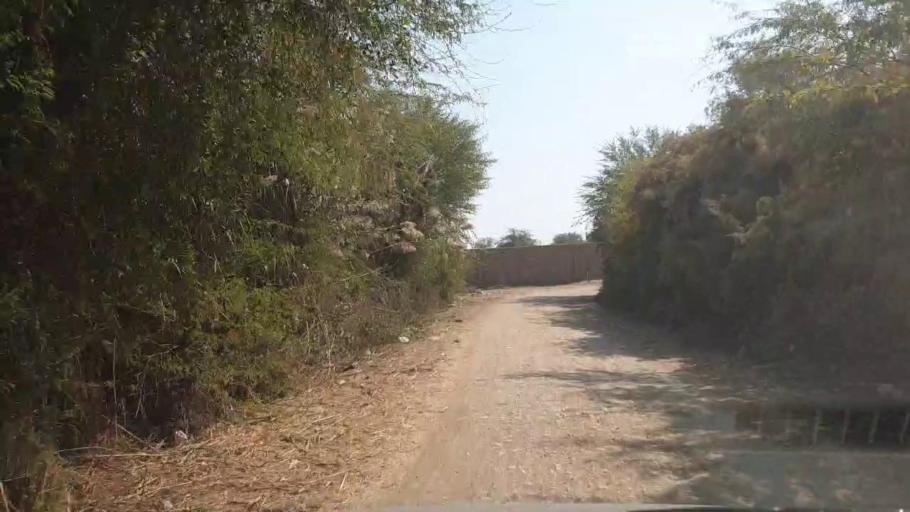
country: PK
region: Sindh
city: Chambar
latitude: 25.3508
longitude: 68.8238
